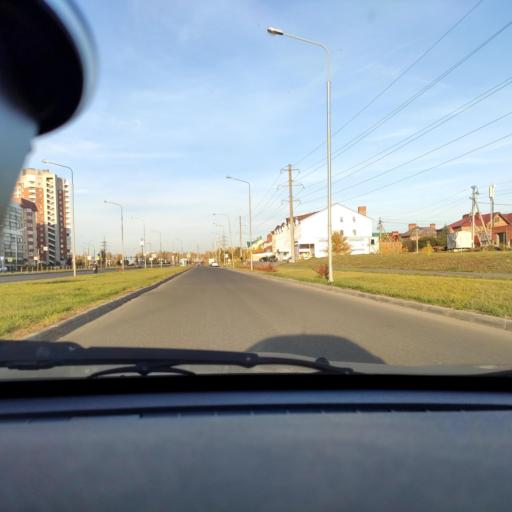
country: RU
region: Samara
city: Tol'yatti
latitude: 53.5430
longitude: 49.3684
